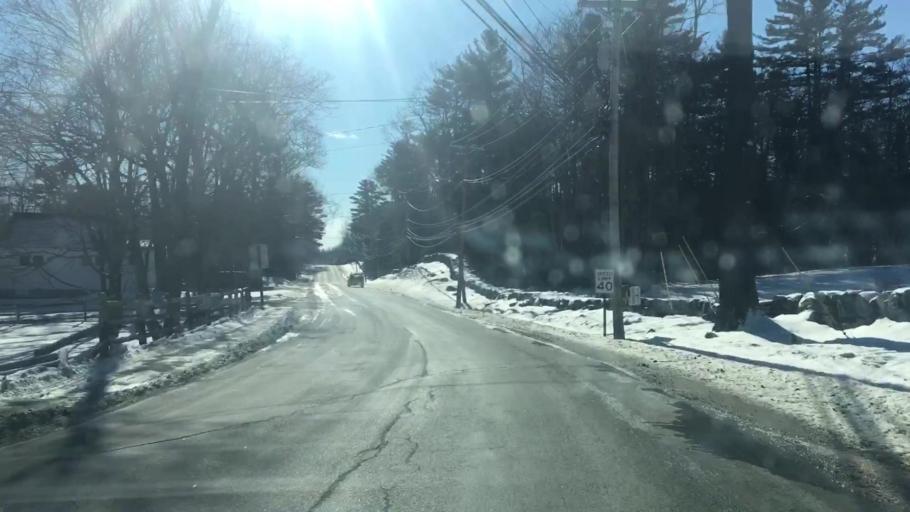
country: US
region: Maine
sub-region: Hancock County
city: Ellsworth
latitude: 44.5375
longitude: -68.4305
